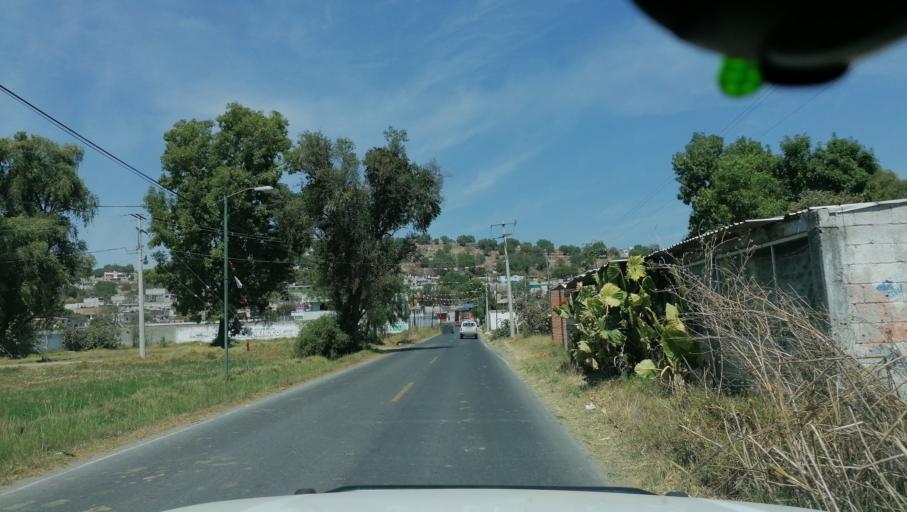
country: MX
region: Tlaxcala
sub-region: Tetlatlahuca
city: Tetlatlahuca
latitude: 19.2291
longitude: -98.2934
